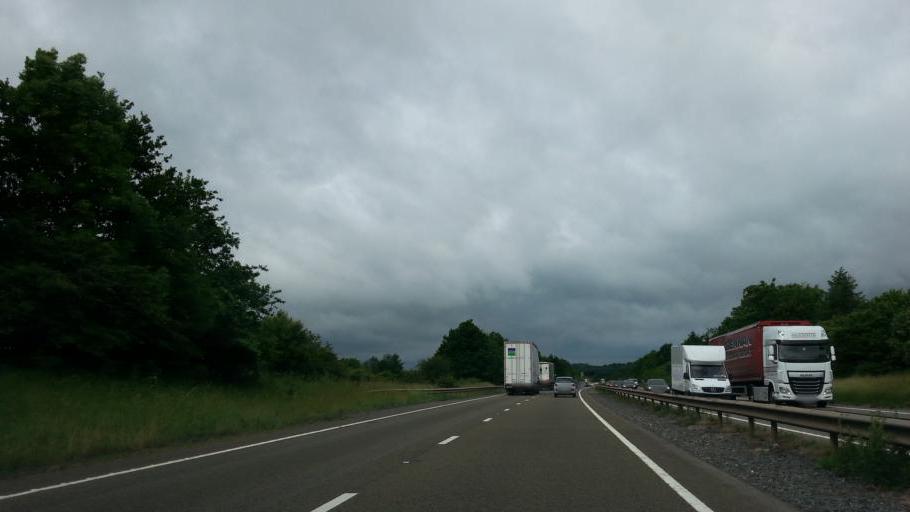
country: GB
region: England
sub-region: Leicestershire
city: Measham
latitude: 52.7085
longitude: -1.5196
